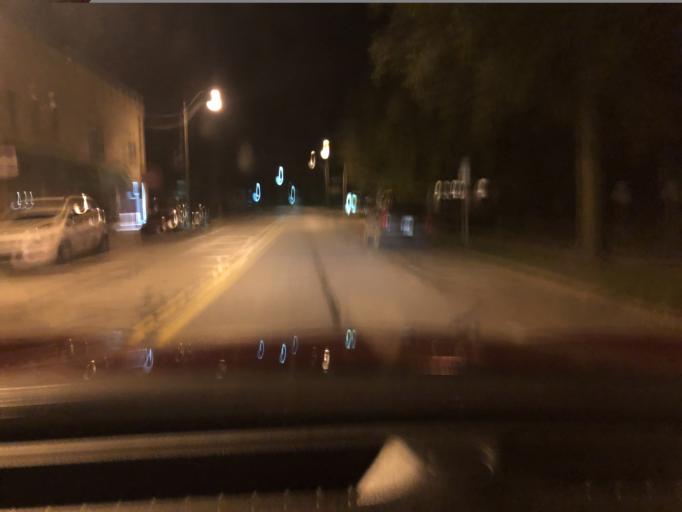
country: US
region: Indiana
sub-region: DeKalb County
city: Auburn
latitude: 41.3654
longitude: -85.0558
